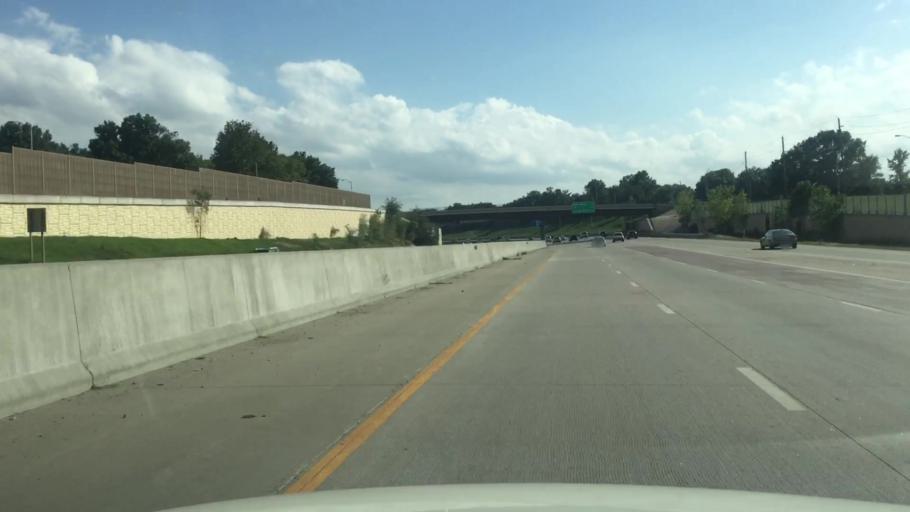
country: US
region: Kansas
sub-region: Johnson County
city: Lenexa
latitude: 38.9658
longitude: -94.7138
